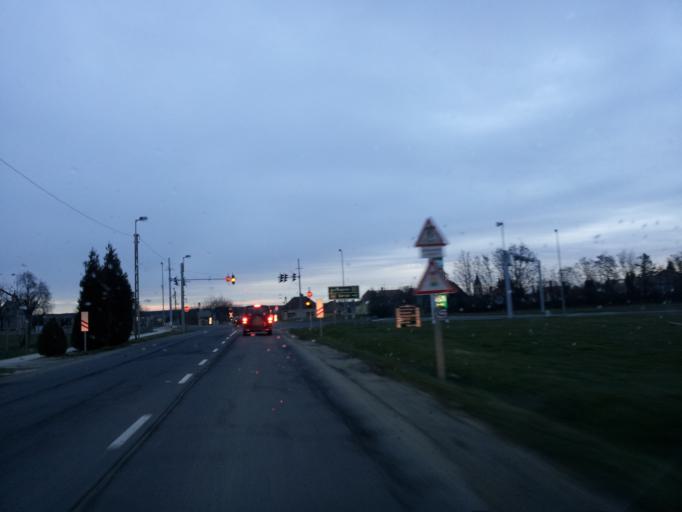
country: HU
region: Vas
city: Buk
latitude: 47.5027
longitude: 16.7800
